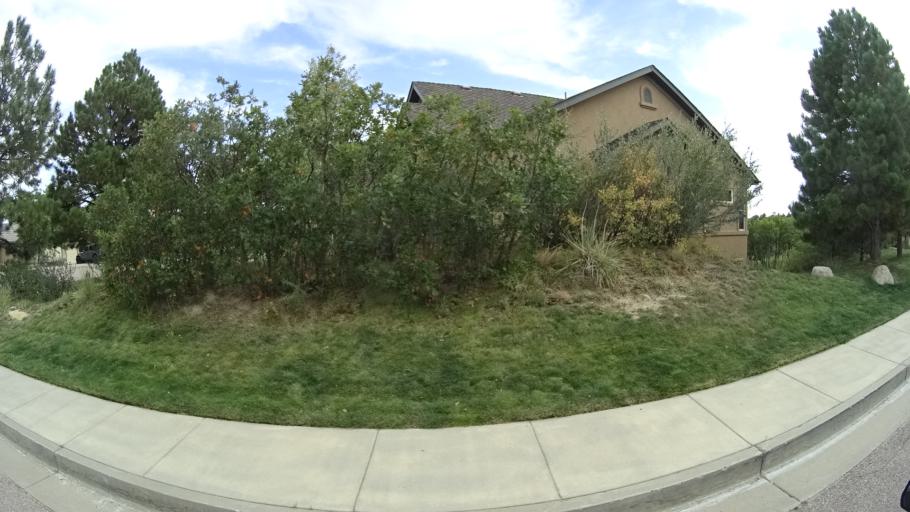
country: US
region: Colorado
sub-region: El Paso County
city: Colorado Springs
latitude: 38.9003
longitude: -104.7901
